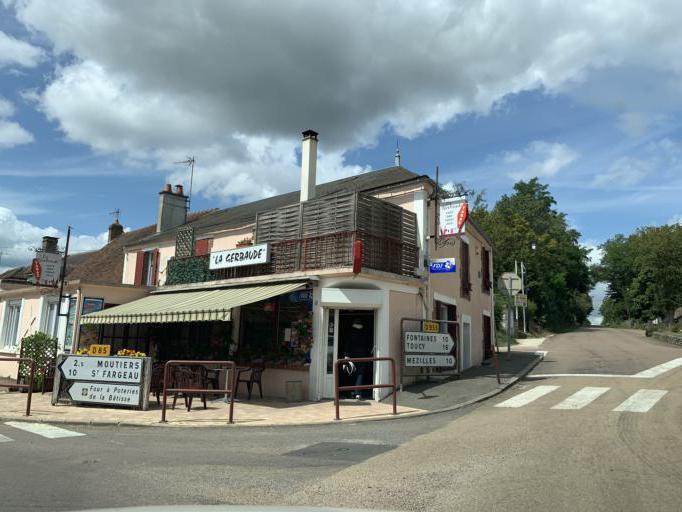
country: FR
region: Bourgogne
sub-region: Departement de l'Yonne
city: Saint-Fargeau
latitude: 47.6199
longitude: 3.1932
